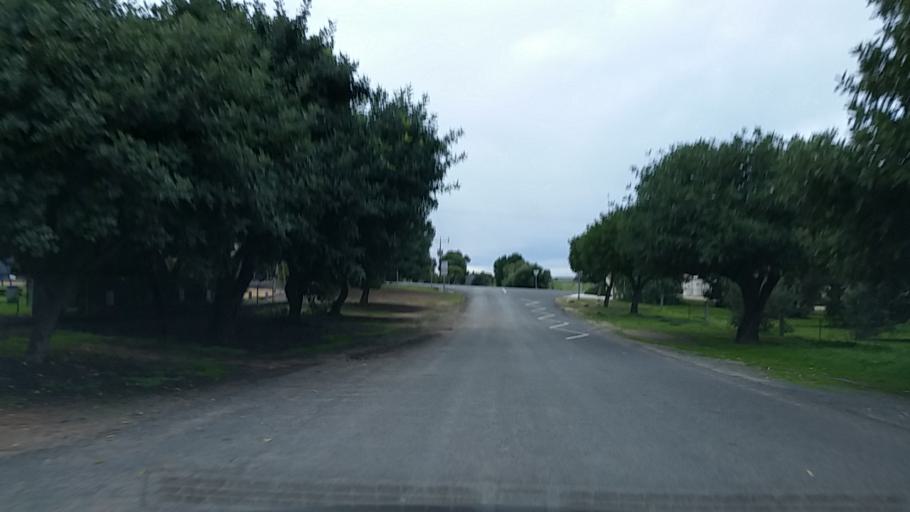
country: AU
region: South Australia
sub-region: Mid Murray
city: Mannum
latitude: -34.8538
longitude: 139.1619
